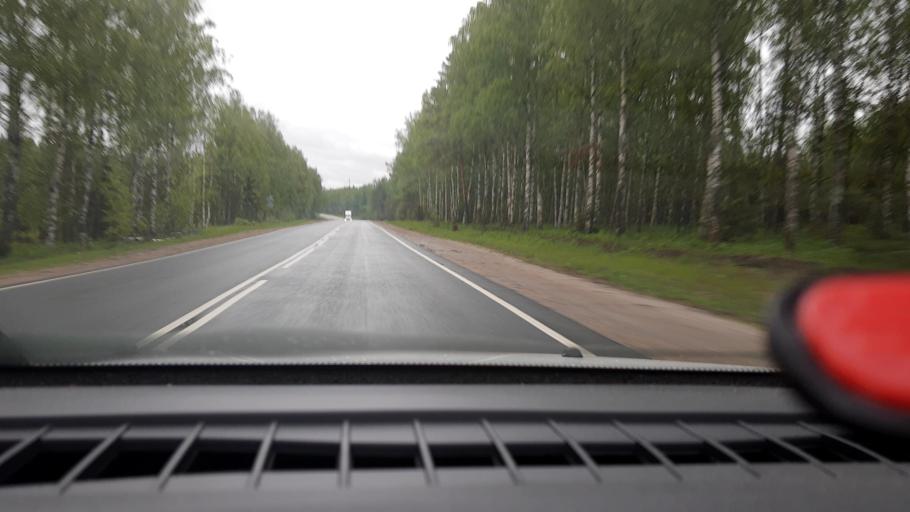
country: RU
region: Nizjnij Novgorod
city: Krasnyye Baki
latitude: 57.0503
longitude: 45.1356
